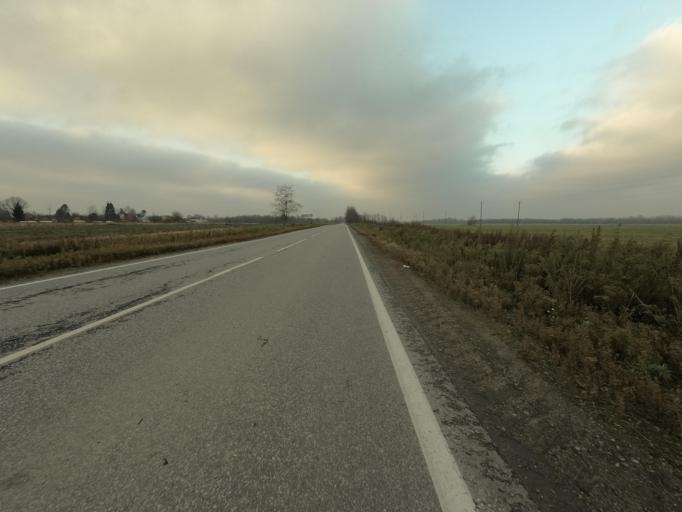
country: RU
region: Leningrad
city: Mga
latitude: 59.7643
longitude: 31.0171
